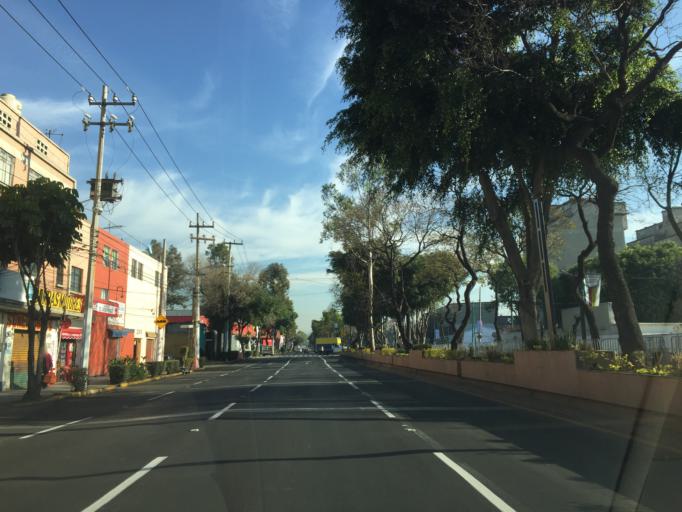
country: MX
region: Mexico City
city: Cuauhtemoc
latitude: 19.4631
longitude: -99.1257
